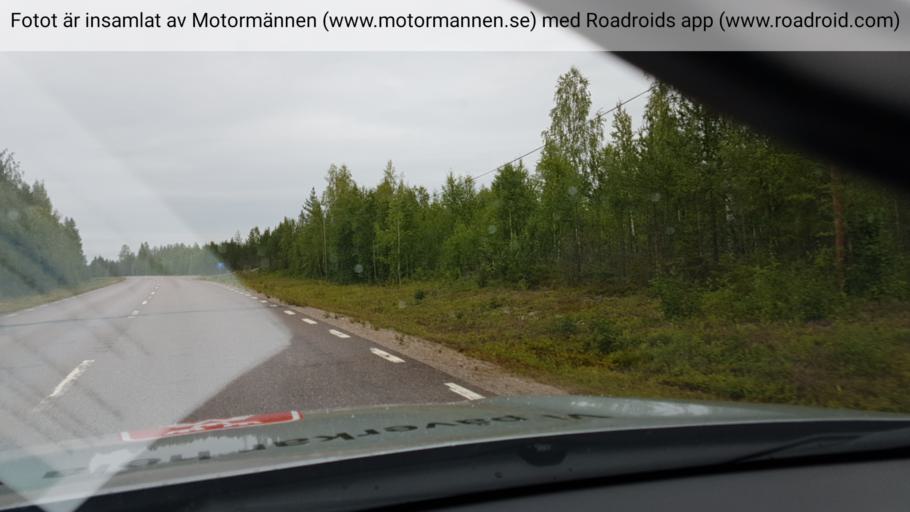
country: SE
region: Norrbotten
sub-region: Alvsbyns Kommun
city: AElvsbyn
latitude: 66.2013
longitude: 20.8810
